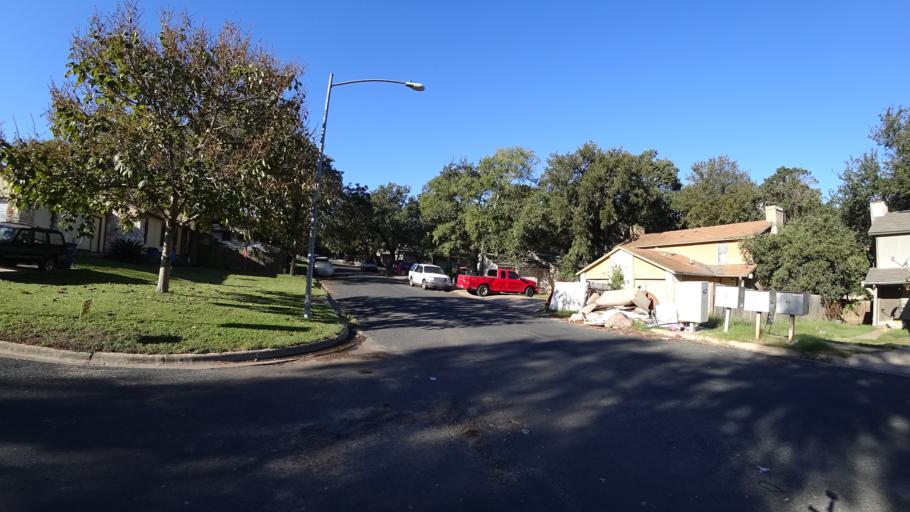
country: US
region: Texas
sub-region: Travis County
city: Austin
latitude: 30.2236
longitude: -97.6675
